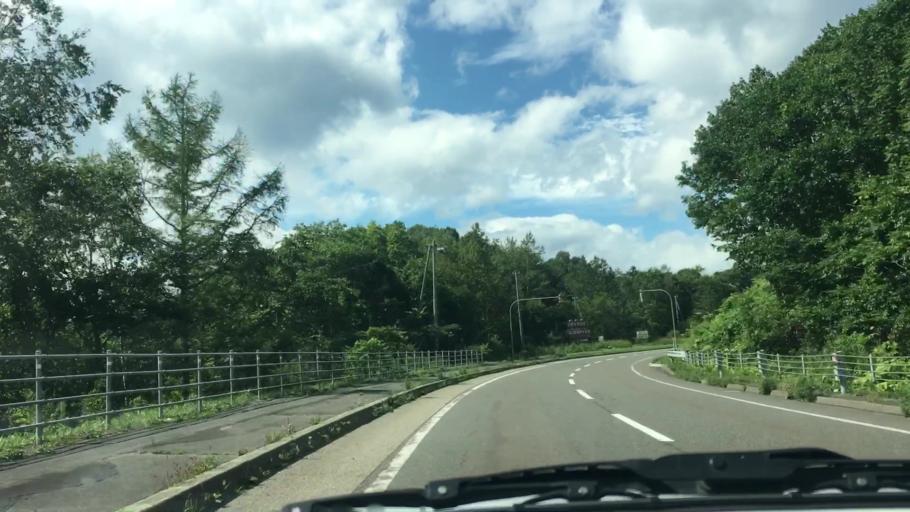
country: JP
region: Hokkaido
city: Otofuke
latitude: 43.3352
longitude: 143.2886
